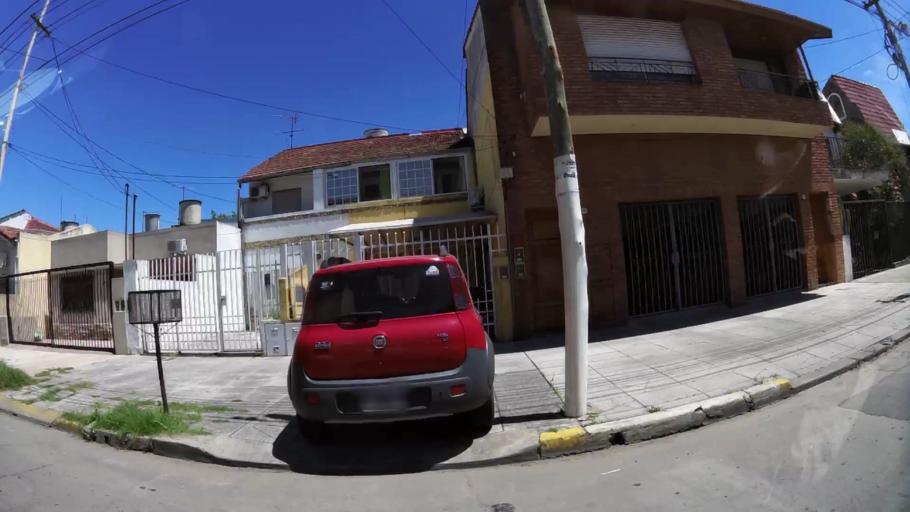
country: AR
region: Buenos Aires
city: Caseros
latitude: -34.5999
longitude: -58.5532
